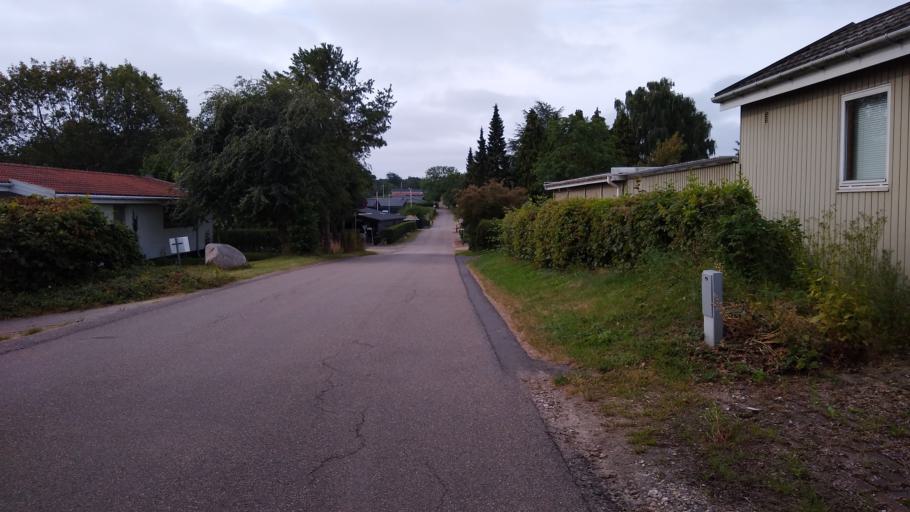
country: DK
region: South Denmark
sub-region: Vejle Kommune
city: Brejning
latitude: 55.6481
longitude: 9.7403
